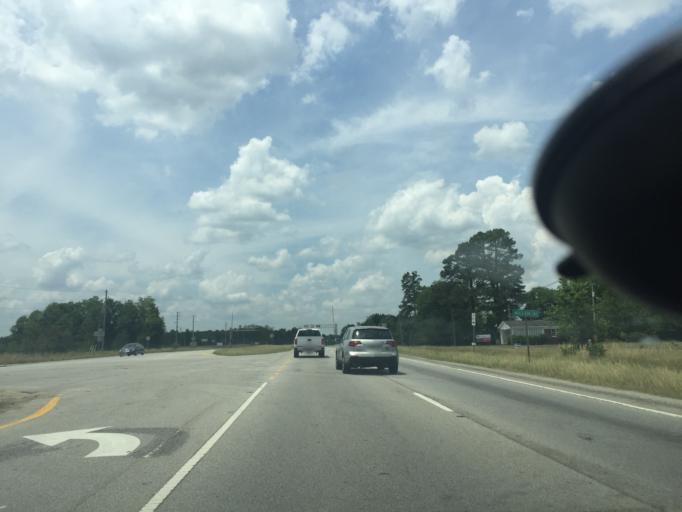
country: US
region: Georgia
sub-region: Bulloch County
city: Statesboro
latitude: 32.4172
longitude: -81.8011
